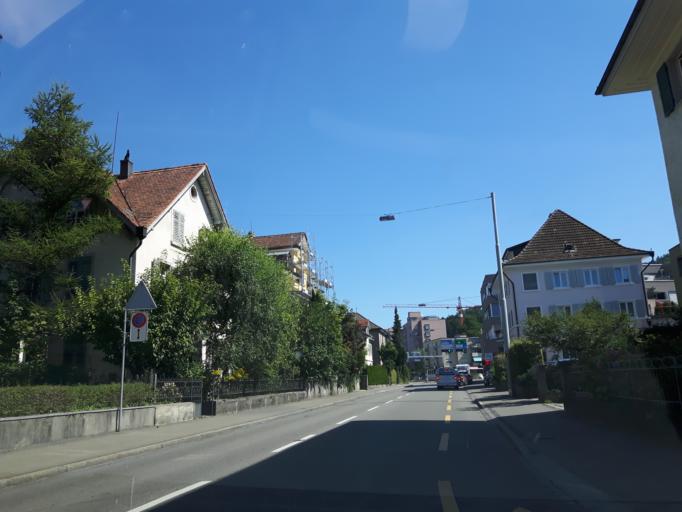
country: CH
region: Zurich
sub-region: Bezirk Zuerich
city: Zuerich (Kreis 12) / Saatlen
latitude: 47.4053
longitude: 8.5553
